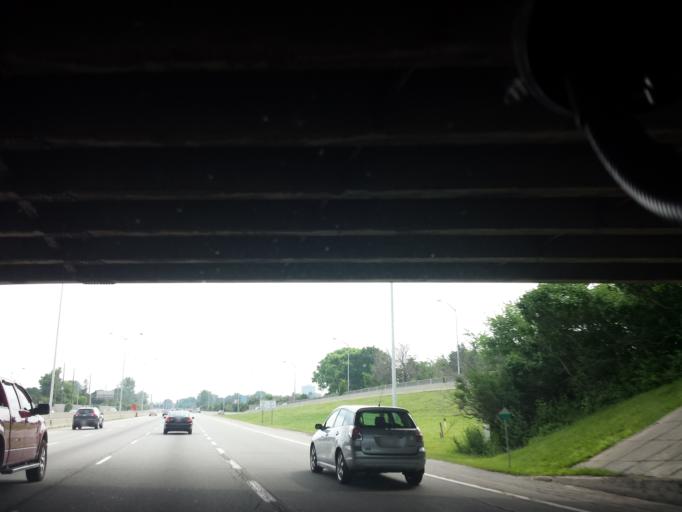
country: CA
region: Ontario
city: Bells Corners
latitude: 45.3610
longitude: -75.7682
